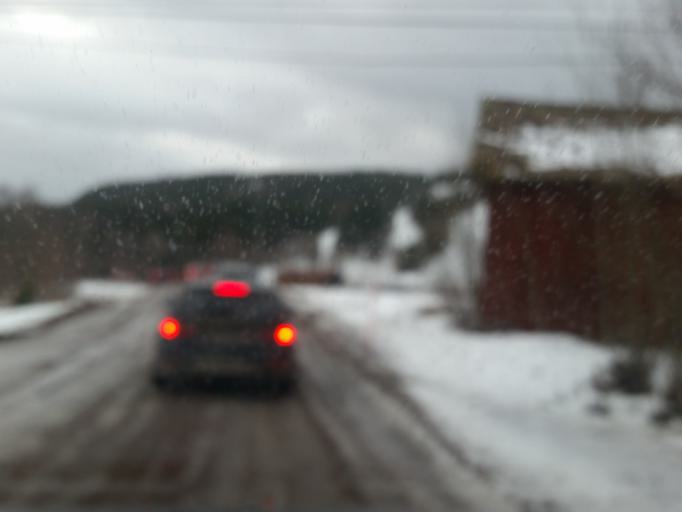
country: SE
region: Gaevleborg
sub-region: Sandvikens Kommun
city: Jarbo
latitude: 60.7621
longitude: 16.5036
